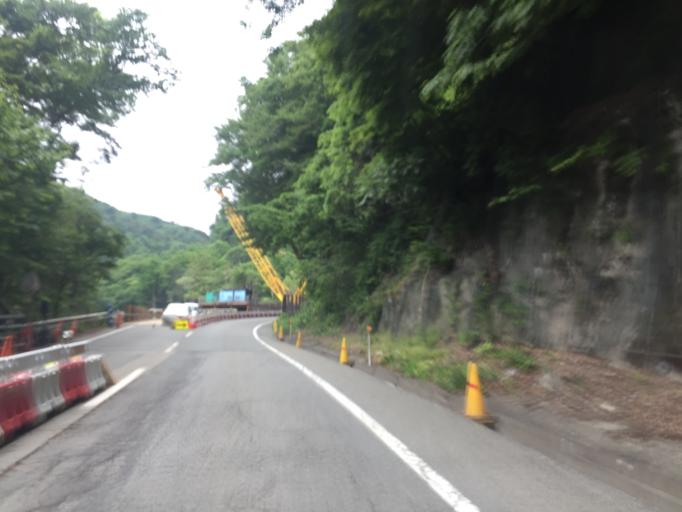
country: JP
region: Fukushima
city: Namie
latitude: 37.4098
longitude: 140.8801
